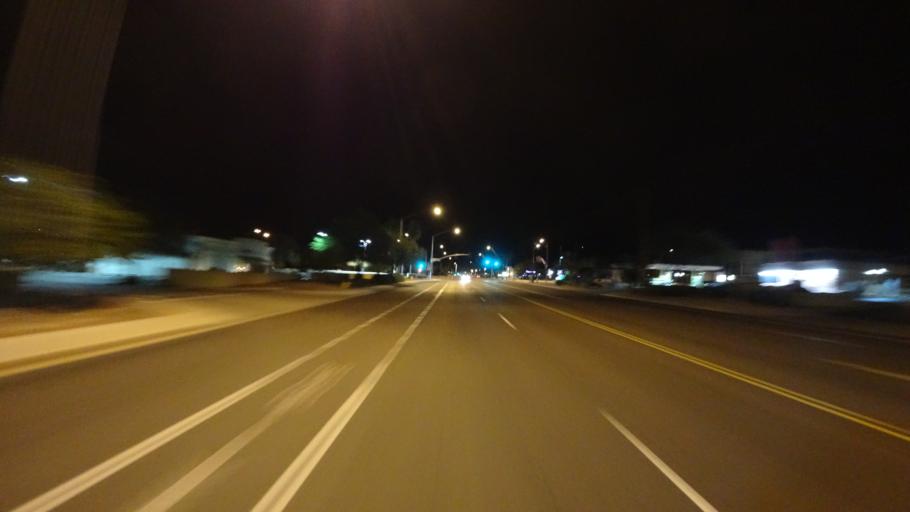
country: US
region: Arizona
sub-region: Maricopa County
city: Mesa
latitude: 33.4509
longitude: -111.7016
